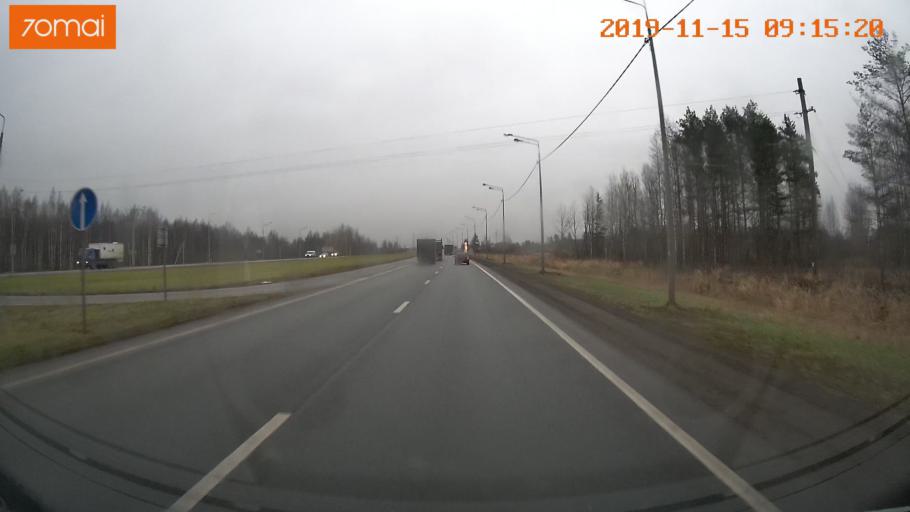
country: RU
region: Vologda
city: Tonshalovo
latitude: 59.2375
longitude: 37.9662
